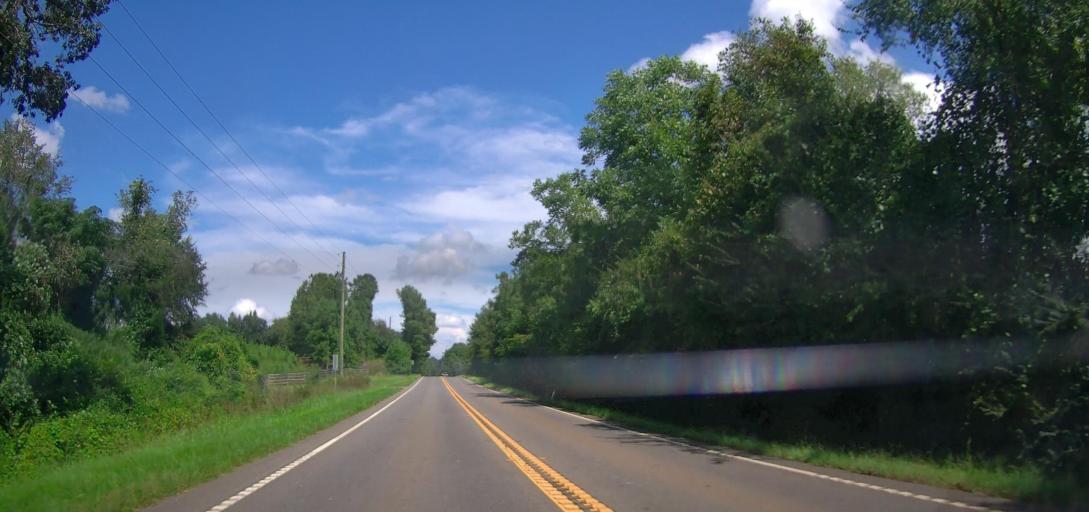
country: US
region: Georgia
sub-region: Macon County
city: Marshallville
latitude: 32.4522
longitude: -83.9642
